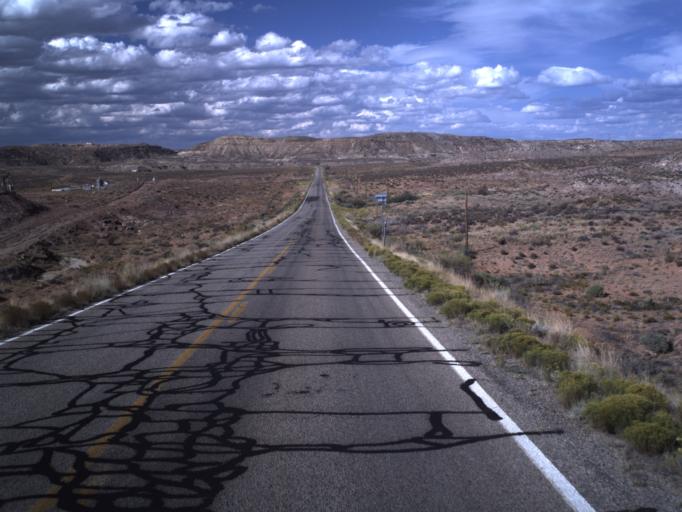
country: US
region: Utah
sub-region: San Juan County
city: Blanding
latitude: 37.2895
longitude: -109.2891
